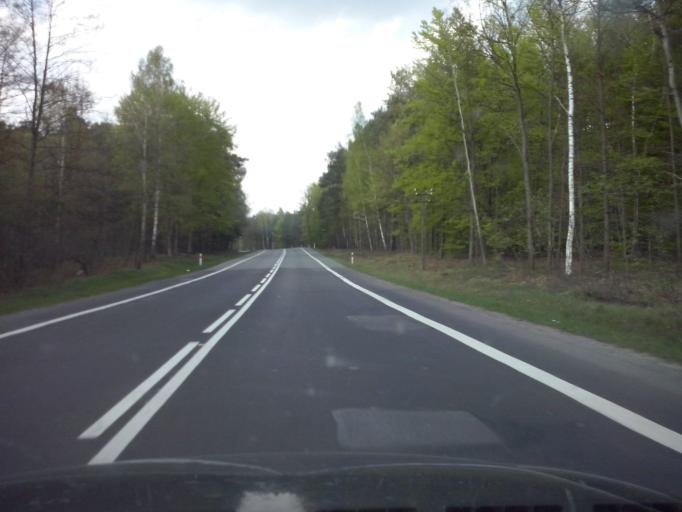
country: PL
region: Subcarpathian Voivodeship
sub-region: Powiat rzeszowski
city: Gorno
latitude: 50.2712
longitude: 22.1410
